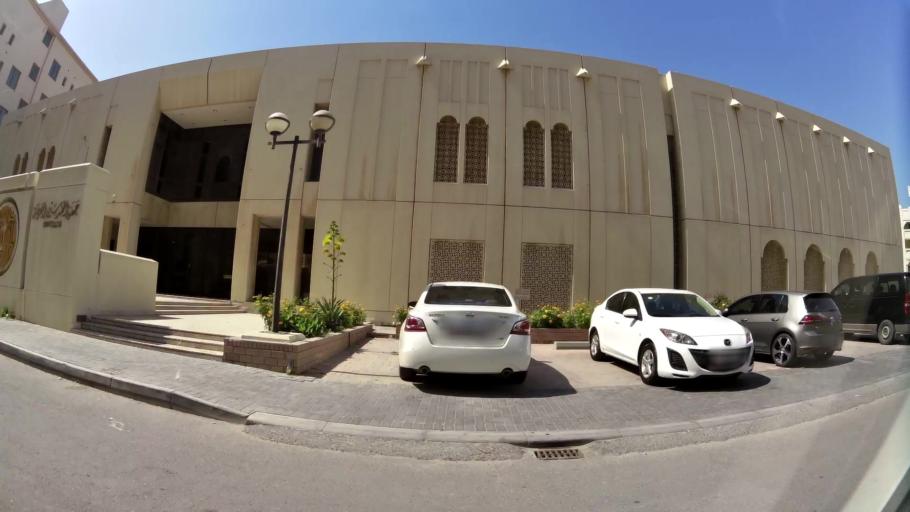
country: BH
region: Manama
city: Manama
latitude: 26.2134
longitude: 50.5980
